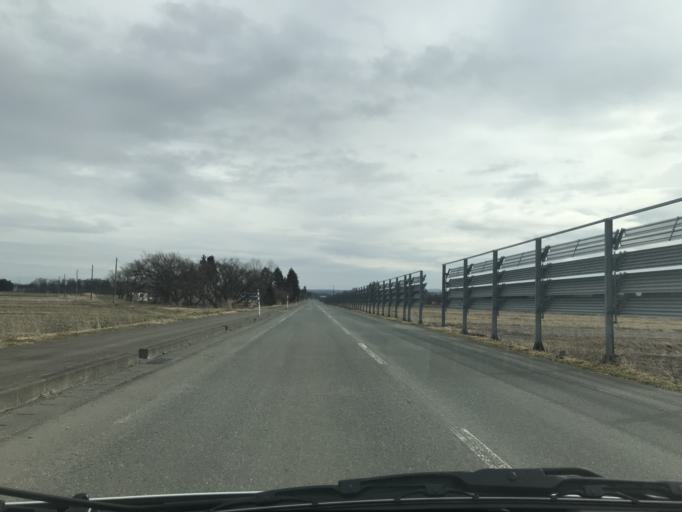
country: JP
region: Iwate
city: Hanamaki
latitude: 39.3366
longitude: 140.9937
